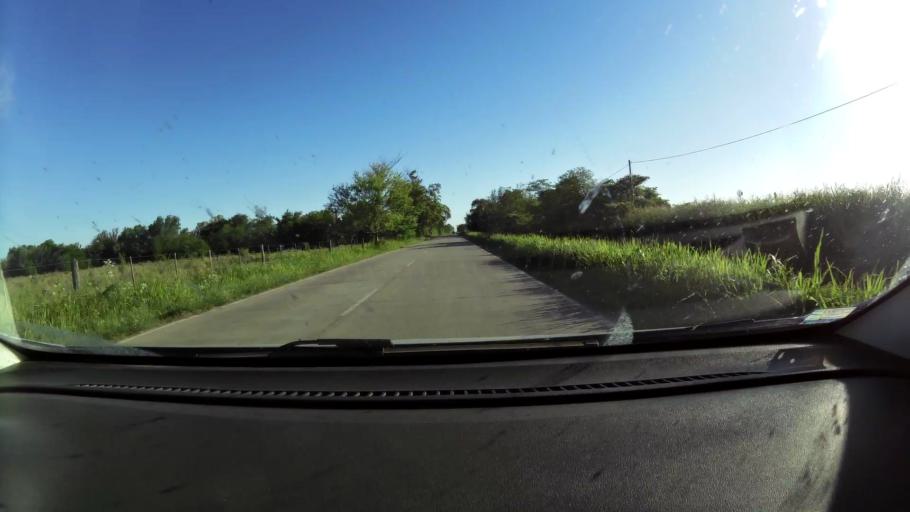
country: AR
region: Cordoba
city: San Francisco
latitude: -31.4484
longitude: -62.1015
